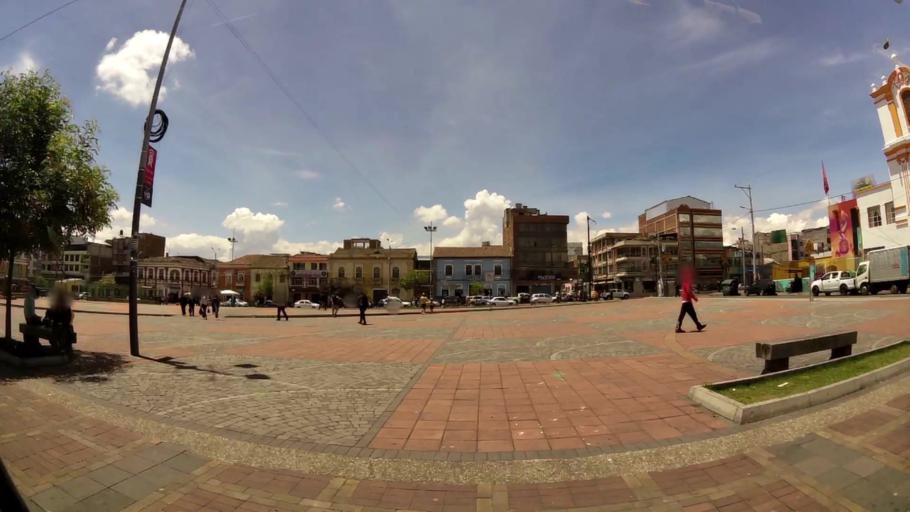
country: EC
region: Chimborazo
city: Riobamba
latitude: -1.6691
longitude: -78.6543
